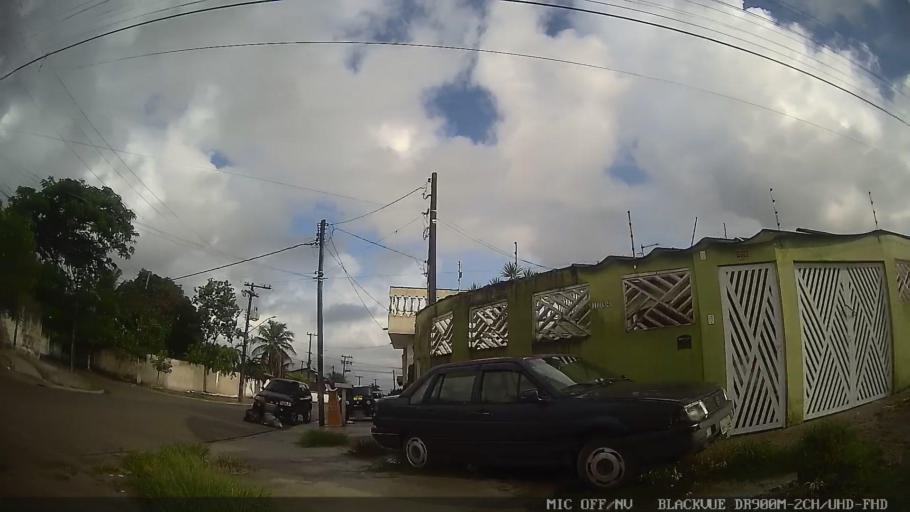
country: BR
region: Sao Paulo
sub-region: Itanhaem
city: Itanhaem
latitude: -24.1802
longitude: -46.8543
